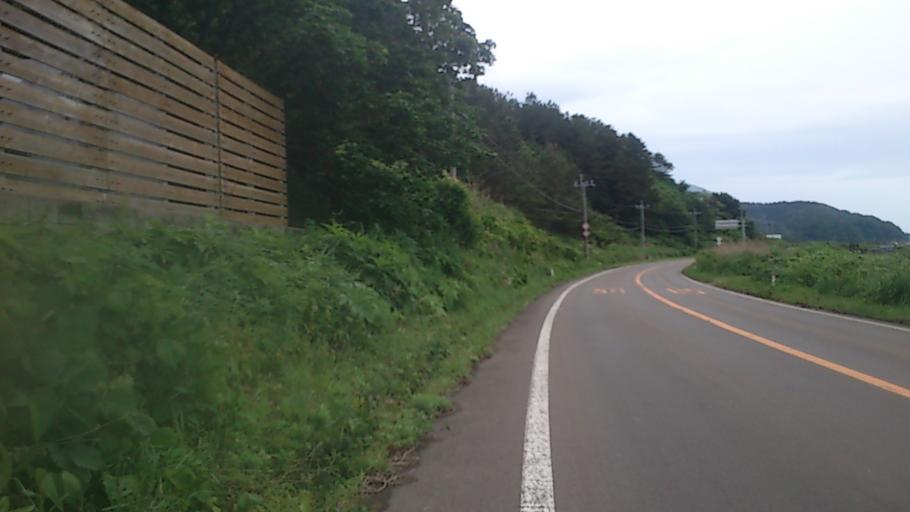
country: JP
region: Akita
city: Noshiromachi
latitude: 40.5026
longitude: 139.9508
